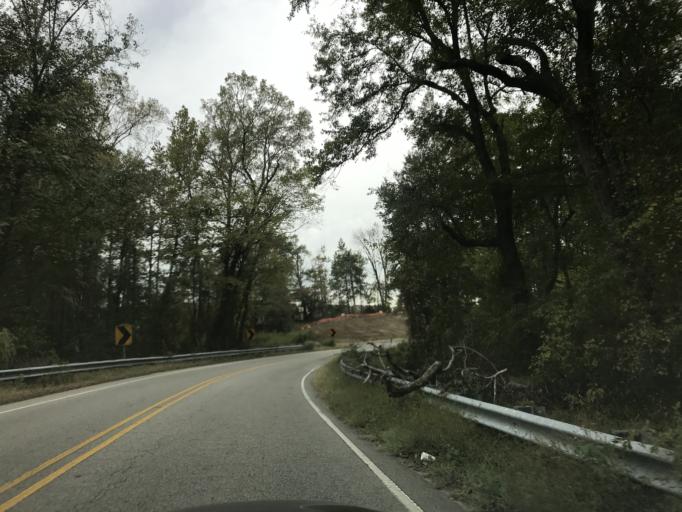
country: US
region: North Carolina
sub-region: Wake County
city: Knightdale
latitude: 35.8332
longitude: -78.5157
